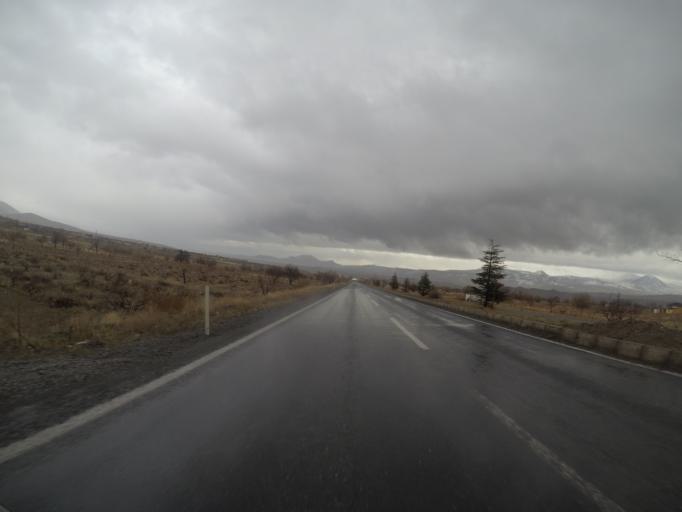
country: TR
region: Kayseri
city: Incesu
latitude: 38.6811
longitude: 35.2071
